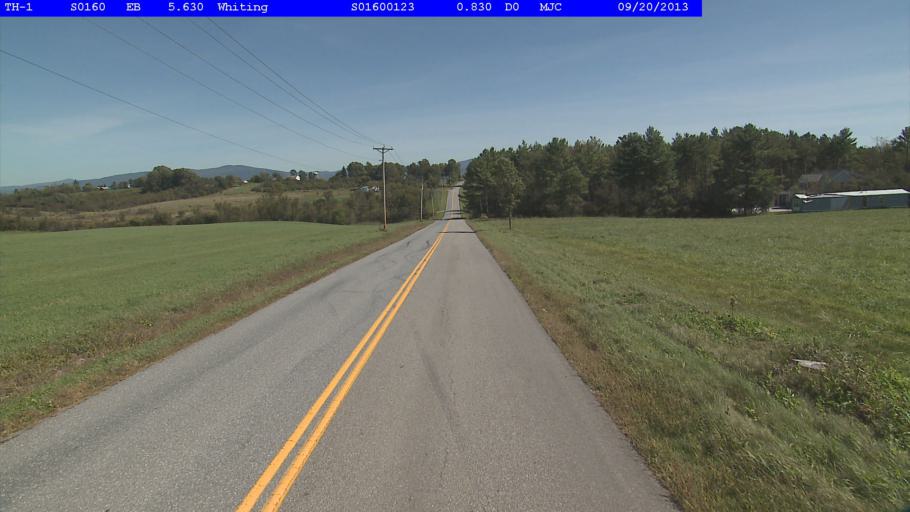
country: US
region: Vermont
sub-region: Rutland County
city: Brandon
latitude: 43.8634
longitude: -73.2091
